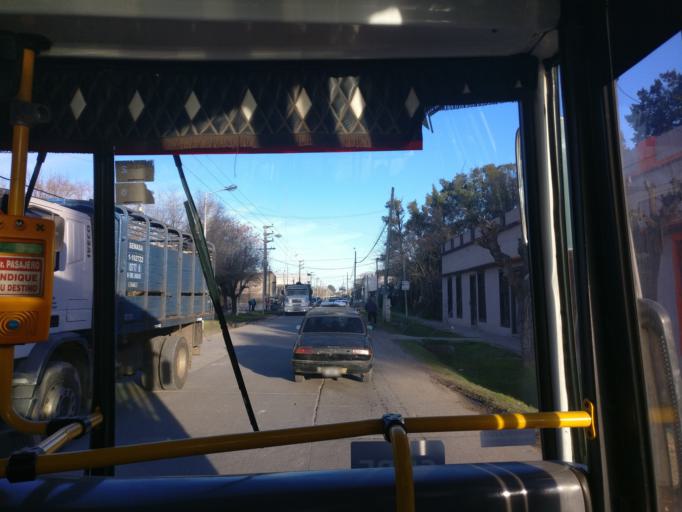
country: AR
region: Buenos Aires
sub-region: Partido de Ezeiza
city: Ezeiza
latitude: -34.9370
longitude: -58.6196
